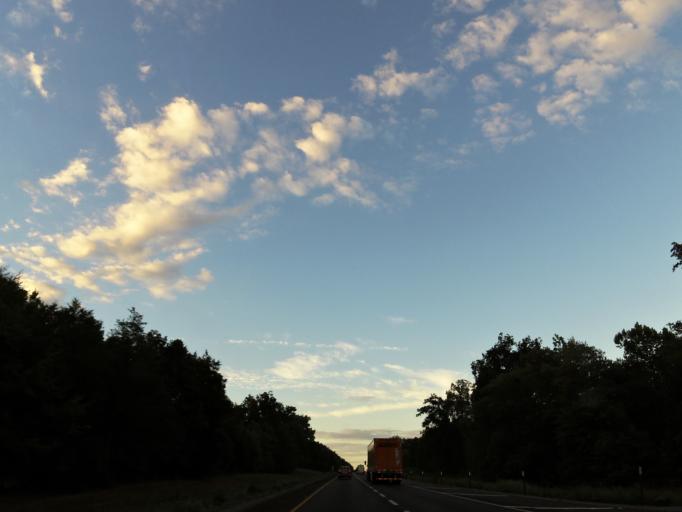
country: US
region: Tennessee
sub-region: Meigs County
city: Decatur
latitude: 35.3468
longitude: -84.7489
